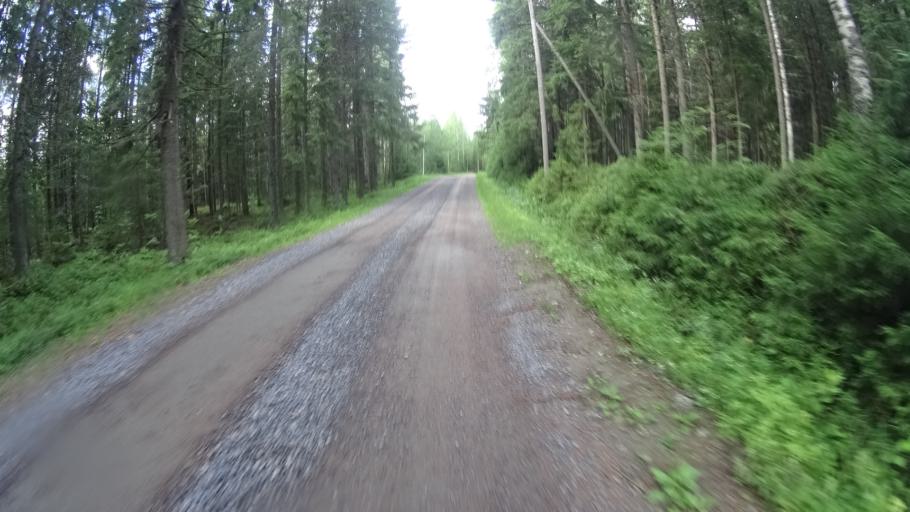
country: FI
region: Uusimaa
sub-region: Helsinki
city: Karkkila
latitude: 60.5991
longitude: 24.2136
